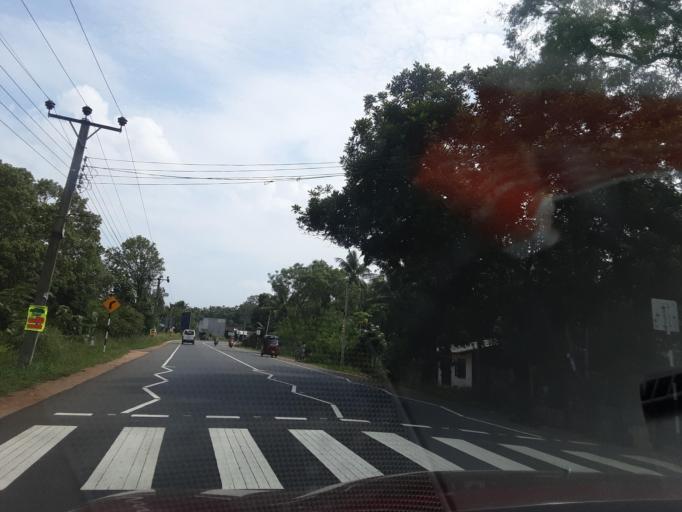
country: LK
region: North Central
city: Anuradhapura
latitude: 8.5031
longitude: 80.5107
